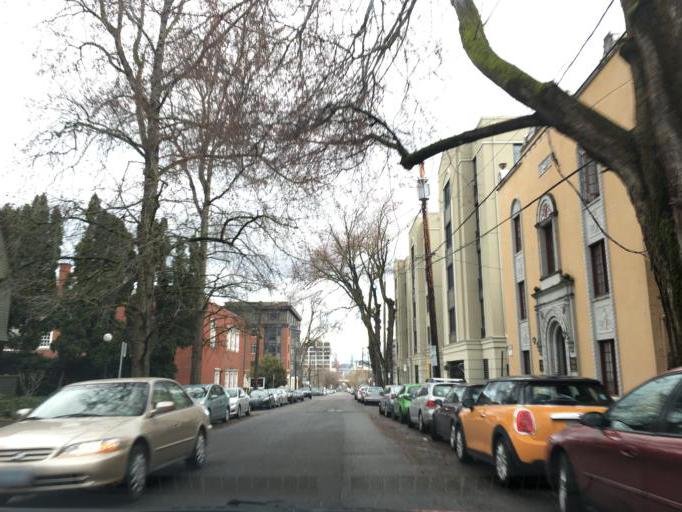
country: US
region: Oregon
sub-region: Multnomah County
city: Portland
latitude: 45.5285
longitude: -122.6918
